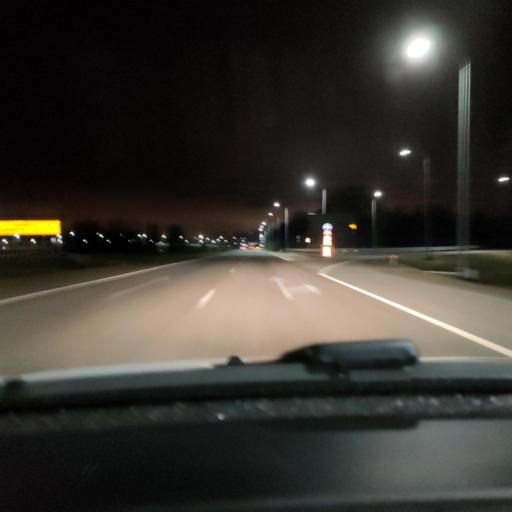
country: RU
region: Voronezj
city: Podgornoye
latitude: 51.8426
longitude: 39.2140
